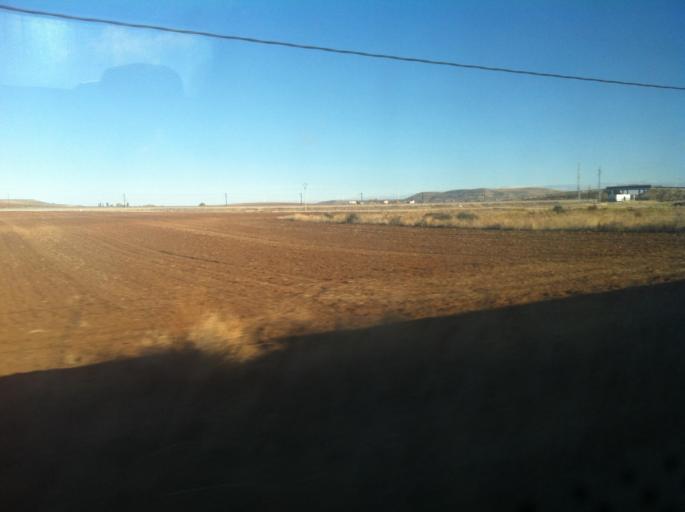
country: ES
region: Castille and Leon
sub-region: Provincia de Burgos
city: Villamedianilla
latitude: 42.1317
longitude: -4.1332
